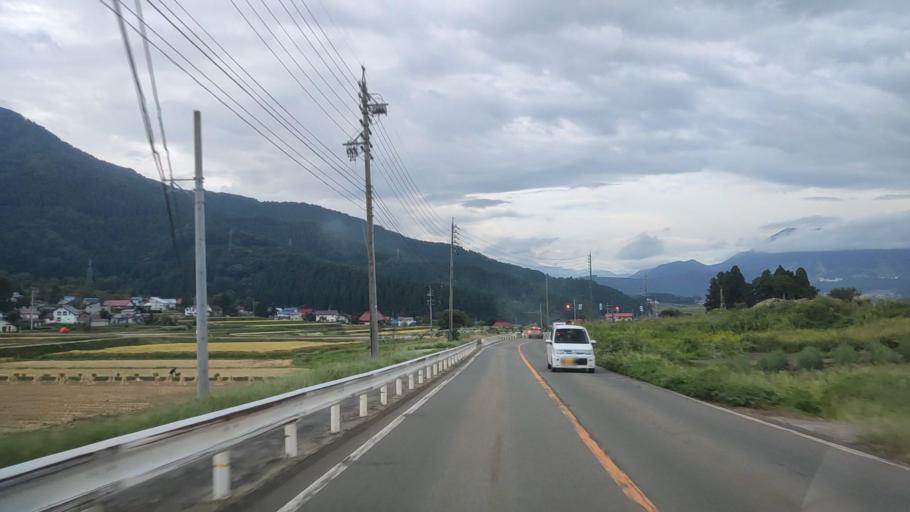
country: JP
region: Nagano
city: Iiyama
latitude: 36.8843
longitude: 138.4121
